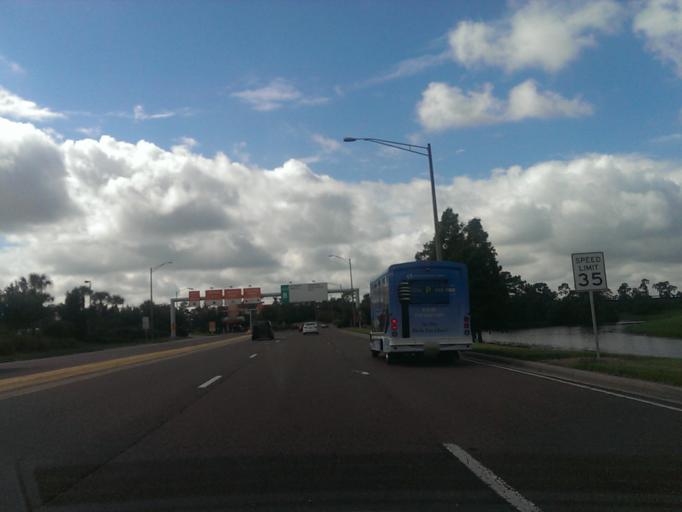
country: US
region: Florida
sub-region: Orange County
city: Belle Isle
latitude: 28.4355
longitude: -81.3105
